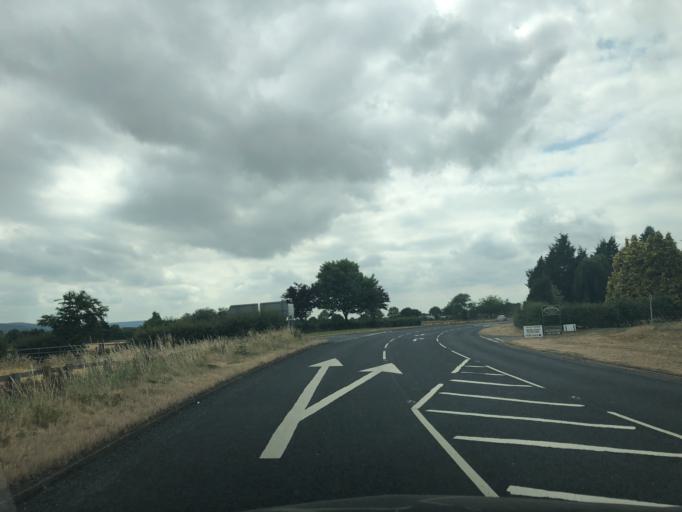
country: GB
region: England
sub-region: North Yorkshire
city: Stokesley
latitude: 54.4719
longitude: -1.1662
